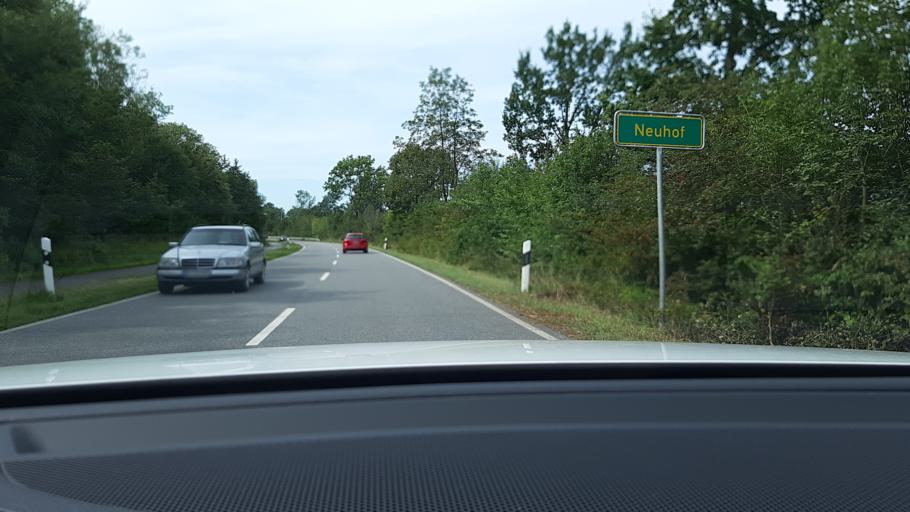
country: DE
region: Schleswig-Holstein
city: Monkhagen
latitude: 53.9106
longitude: 10.5399
